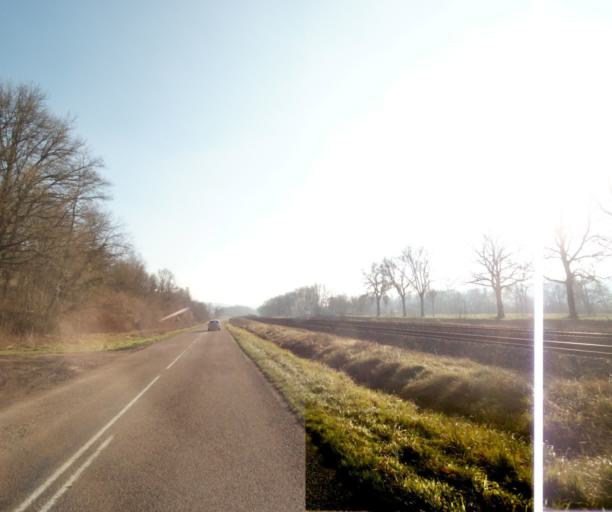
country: FR
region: Champagne-Ardenne
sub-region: Departement de la Haute-Marne
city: Chevillon
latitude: 48.5082
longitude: 5.1235
